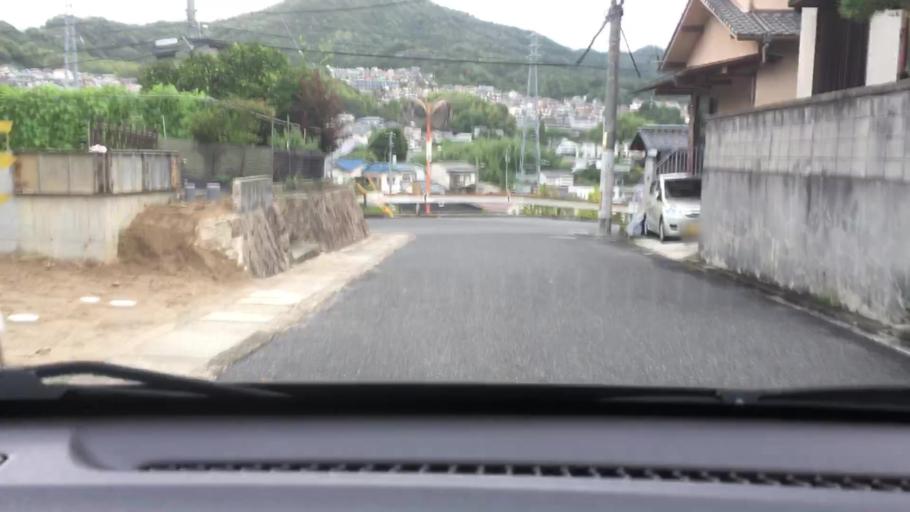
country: JP
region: Hiroshima
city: Hiroshima-shi
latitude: 34.4052
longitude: 132.4180
